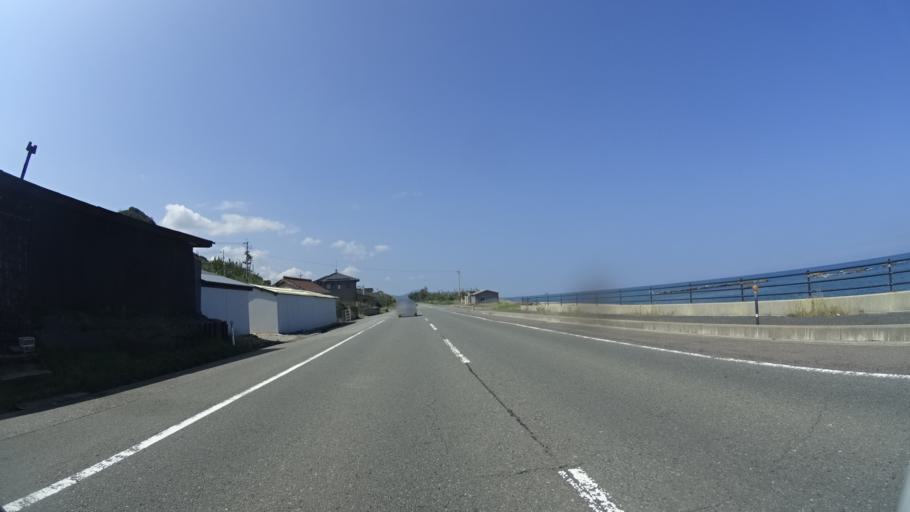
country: JP
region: Shimane
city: Masuda
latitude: 34.6854
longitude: 131.7856
